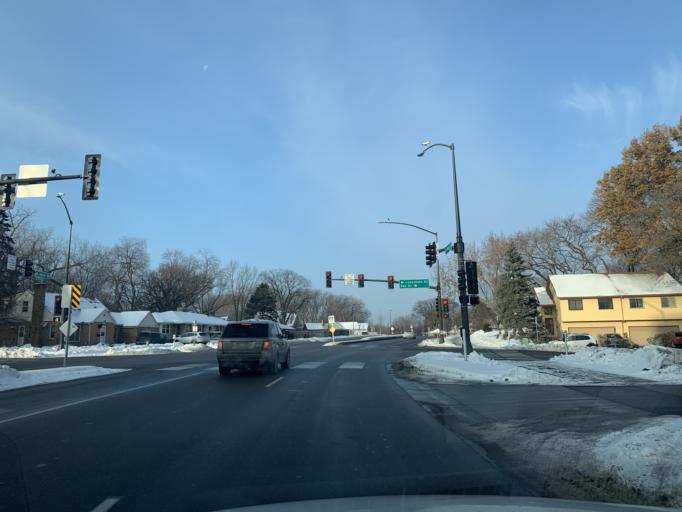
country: US
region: Minnesota
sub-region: Hennepin County
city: Richfield
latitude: 44.8830
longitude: -93.2906
